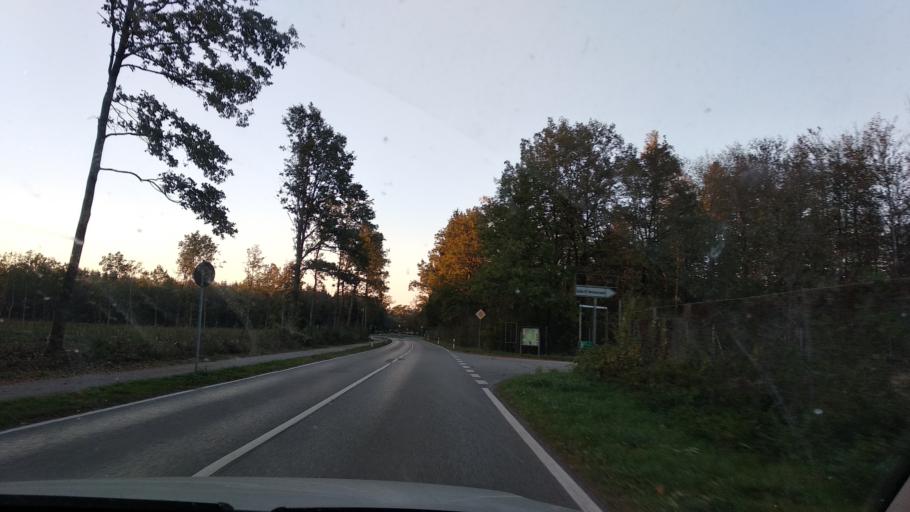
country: DE
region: Bavaria
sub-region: Upper Bavaria
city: Hohenkirchen-Siegertsbrunn
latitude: 48.0350
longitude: 11.7154
